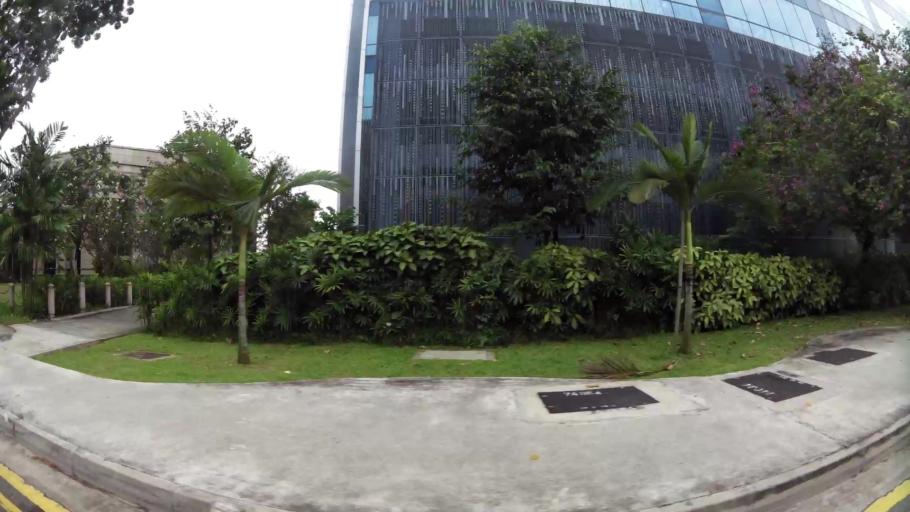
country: SG
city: Singapore
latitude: 1.2908
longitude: 103.7874
